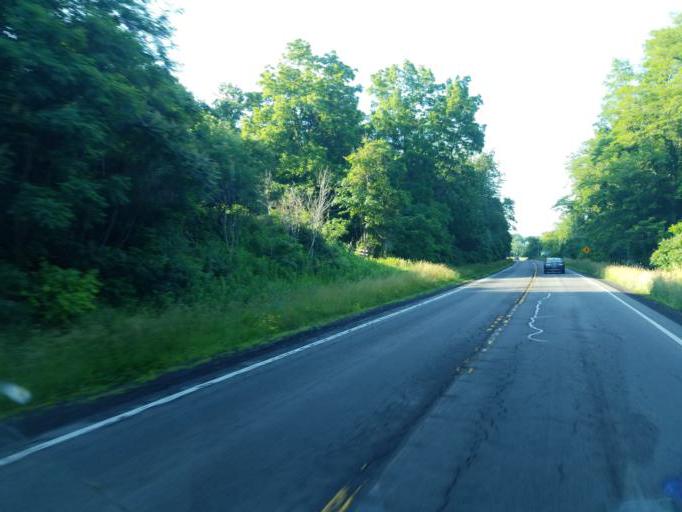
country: US
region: New York
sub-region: Wayne County
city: Clyde
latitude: 43.0485
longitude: -76.8652
